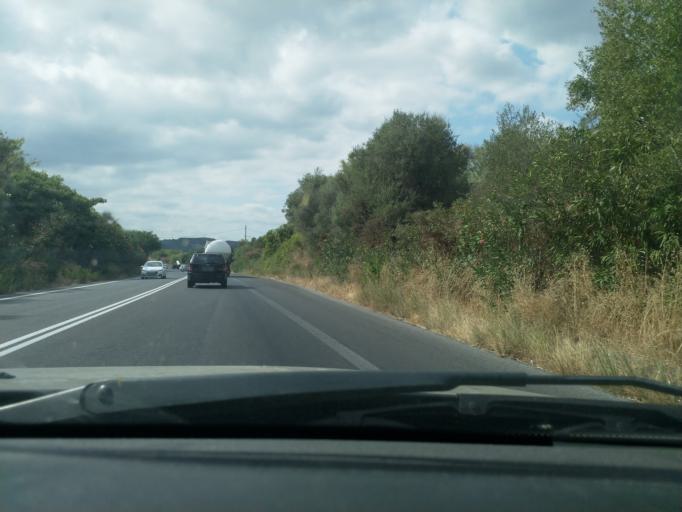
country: GR
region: Crete
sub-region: Nomos Chanias
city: Georgioupolis
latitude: 35.3609
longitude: 24.2494
